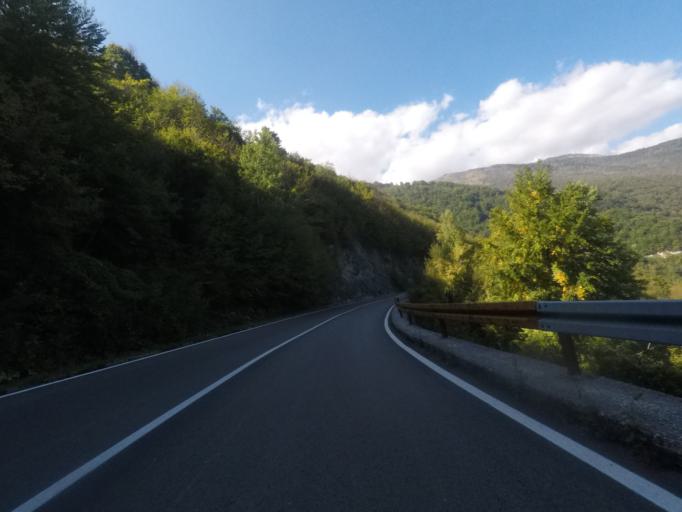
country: ME
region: Opstina Pluzine
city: Pluzine
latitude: 43.0973
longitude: 18.8298
